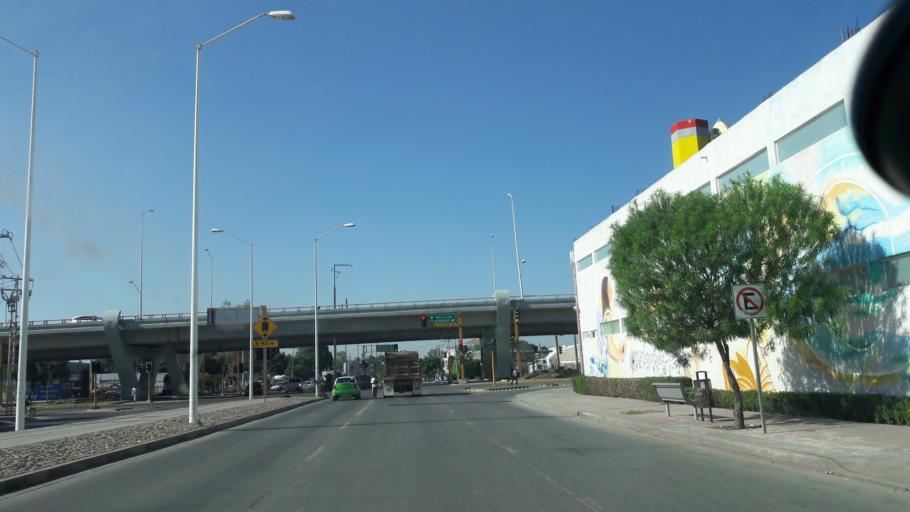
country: MX
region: Guanajuato
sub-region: Leon
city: Medina
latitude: 21.1720
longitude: -101.6571
